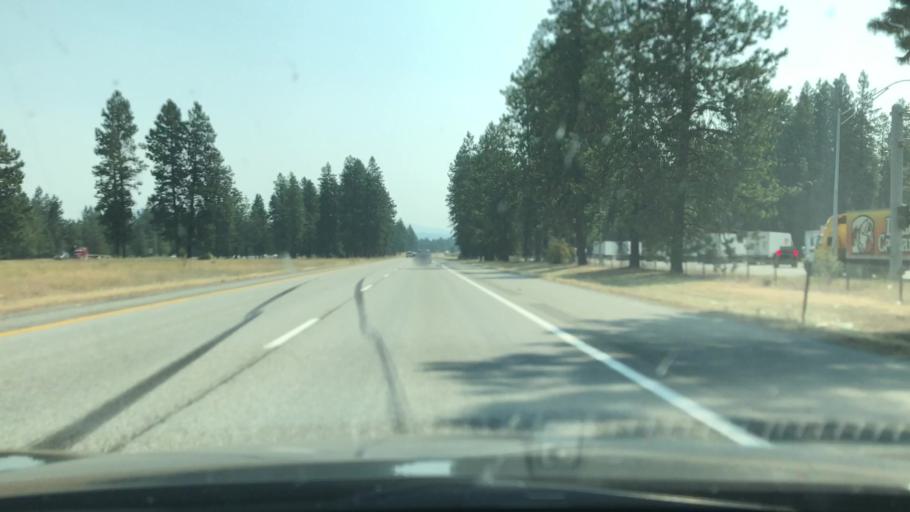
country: US
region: Idaho
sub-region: Kootenai County
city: Post Falls
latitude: 47.7085
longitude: -116.8669
